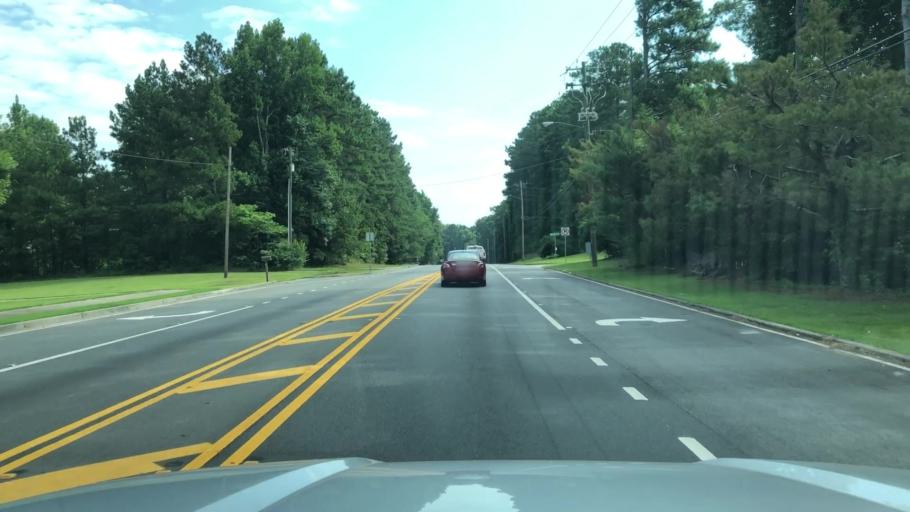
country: US
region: Georgia
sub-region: Cobb County
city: Acworth
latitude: 34.0469
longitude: -84.7271
